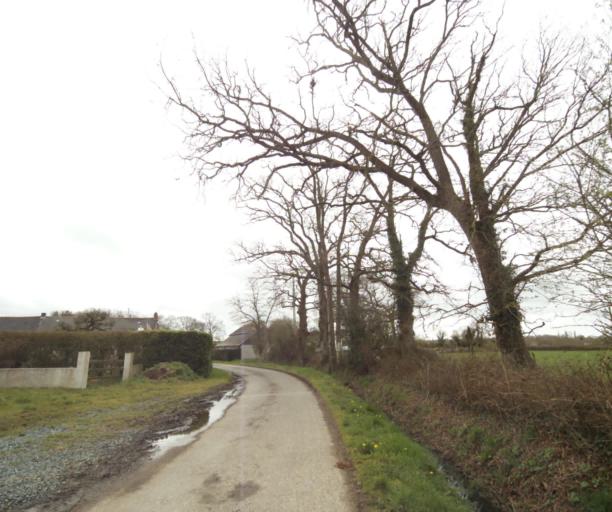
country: FR
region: Pays de la Loire
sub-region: Departement de la Loire-Atlantique
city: Bouvron
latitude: 47.4290
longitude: -1.8744
